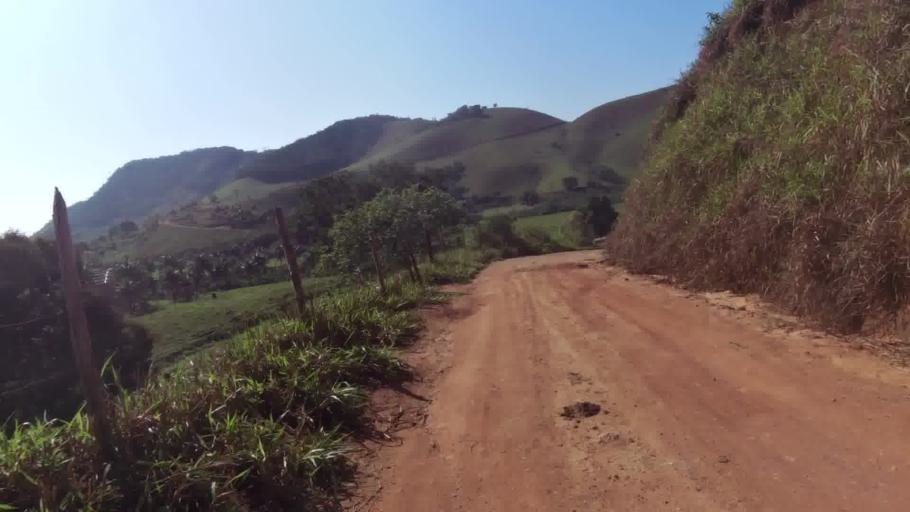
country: BR
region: Espirito Santo
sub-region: Alfredo Chaves
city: Alfredo Chaves
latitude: -20.6813
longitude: -40.7739
